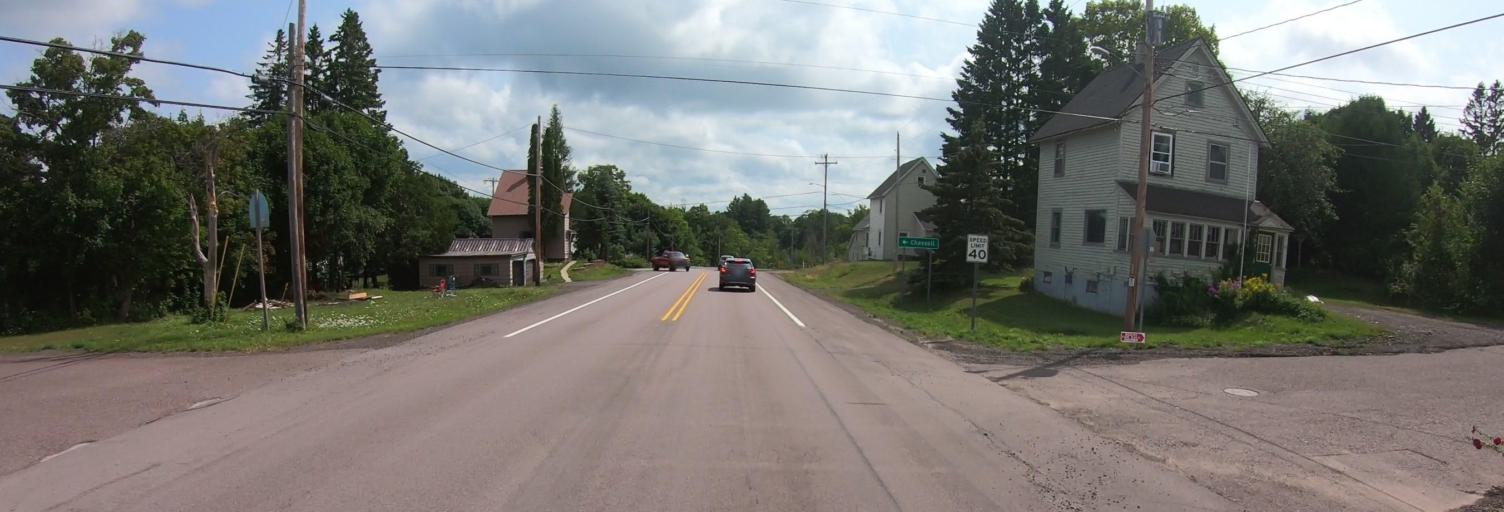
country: US
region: Michigan
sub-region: Houghton County
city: Hancock
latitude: 47.0413
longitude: -88.6725
